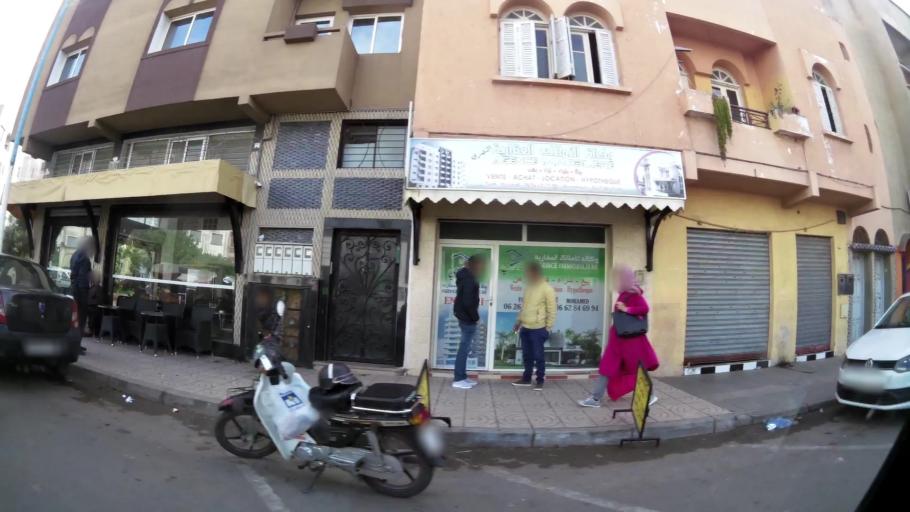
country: MA
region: Doukkala-Abda
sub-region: El-Jadida
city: El Jadida
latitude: 33.2429
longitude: -8.5254
